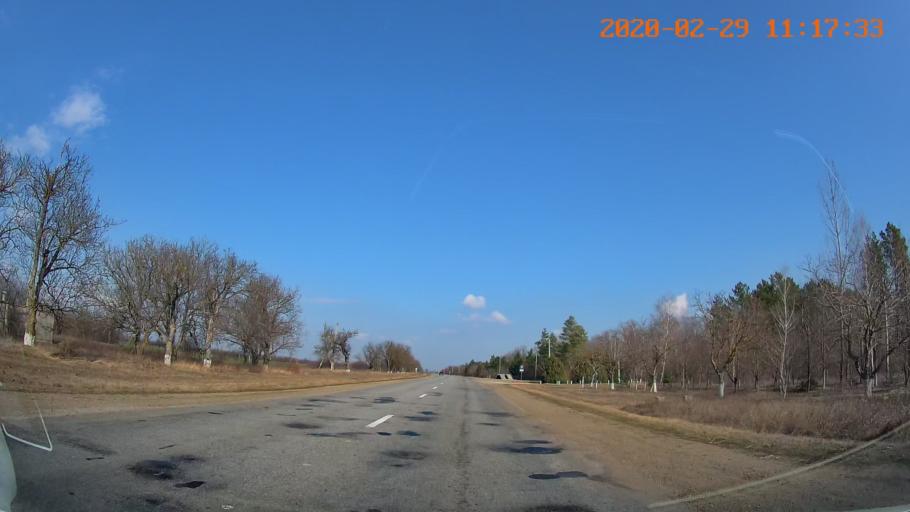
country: MD
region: Telenesti
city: Dubasari
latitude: 47.3233
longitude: 29.1709
